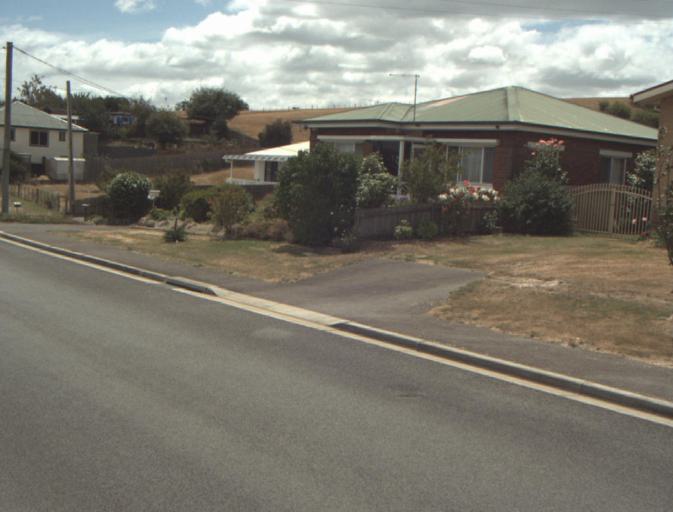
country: AU
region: Tasmania
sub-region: Launceston
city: Newstead
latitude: -41.4646
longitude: 147.2049
